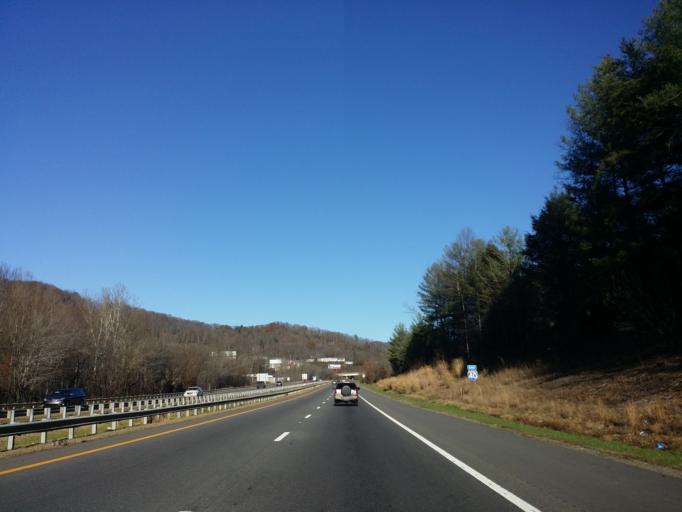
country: US
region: North Carolina
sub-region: Buncombe County
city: Swannanoa
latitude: 35.5853
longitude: -82.4566
